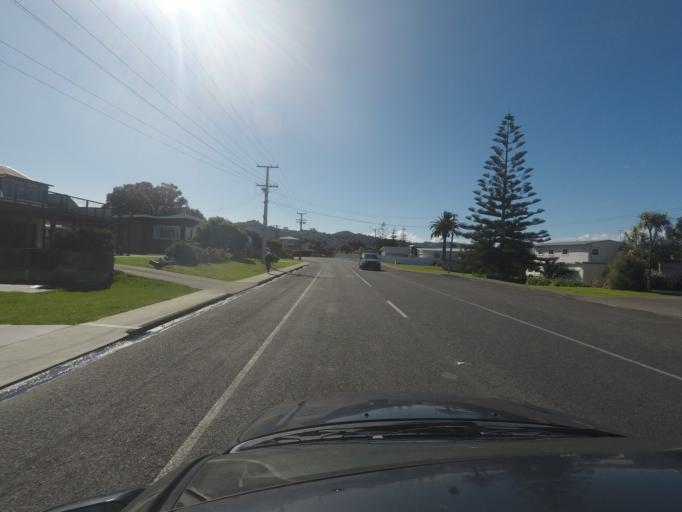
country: NZ
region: Bay of Plenty
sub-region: Western Bay of Plenty District
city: Waihi Beach
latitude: -37.4132
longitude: 175.9463
